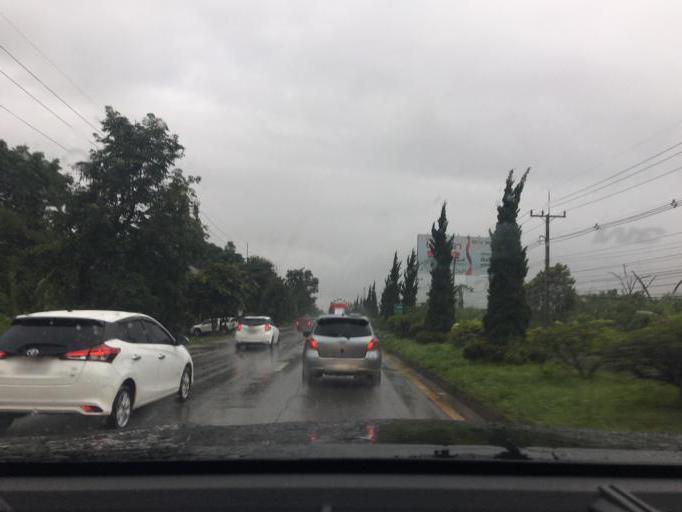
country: TH
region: Chiang Rai
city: Chiang Rai
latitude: 20.0152
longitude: 99.8696
